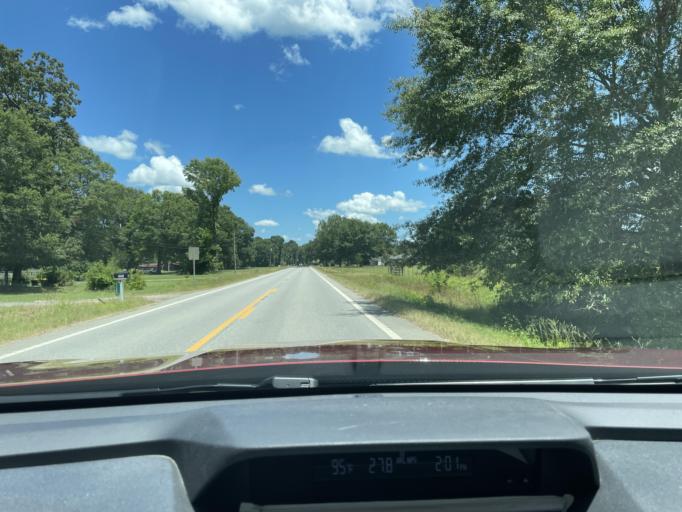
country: US
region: Arkansas
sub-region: Drew County
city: Monticello
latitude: 33.6045
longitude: -91.7305
